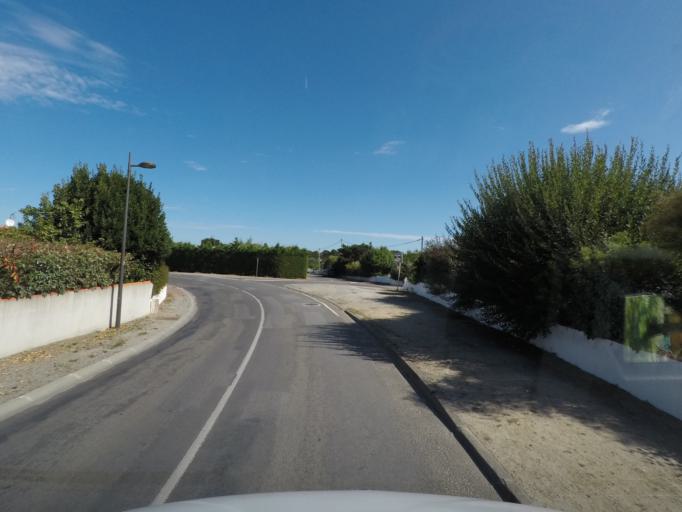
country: FR
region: Pays de la Loire
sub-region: Departement de la Vendee
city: La Gueriniere
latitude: 47.0006
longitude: -2.2267
